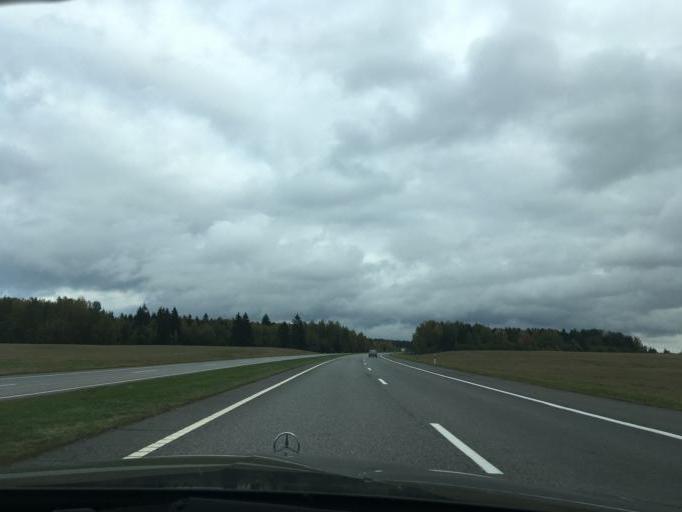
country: BY
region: Vitebsk
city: Talachyn
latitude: 54.4794
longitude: 29.8357
